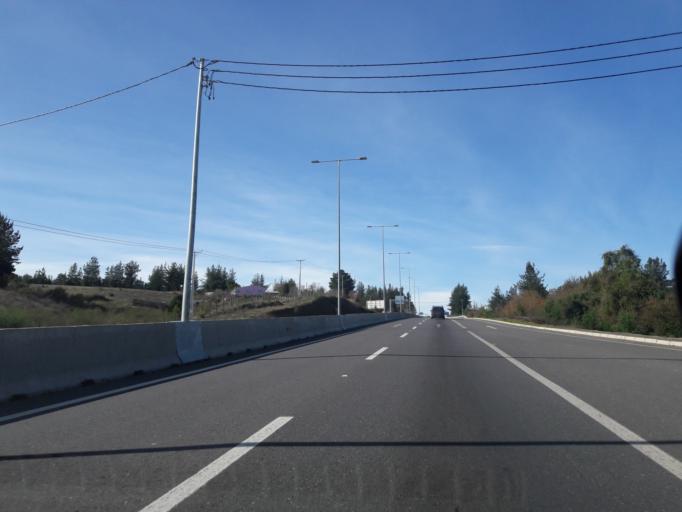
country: CL
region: Biobio
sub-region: Provincia de Biobio
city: Yumbel
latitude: -36.9621
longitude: -72.7182
